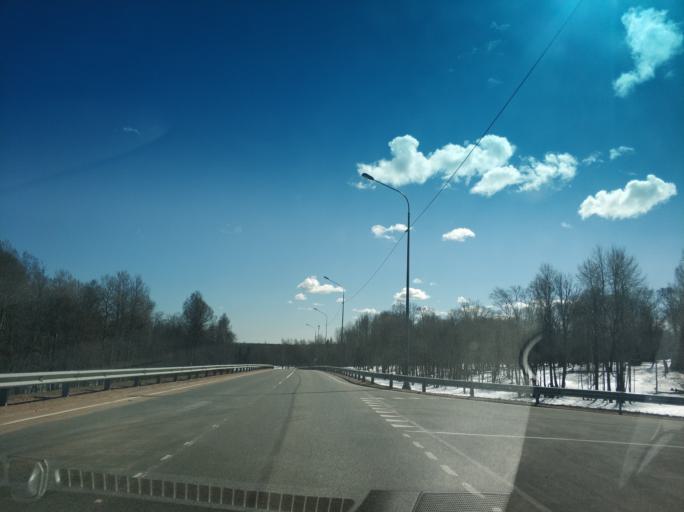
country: RU
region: Leningrad
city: Sosnovo
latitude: 60.4326
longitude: 30.2367
